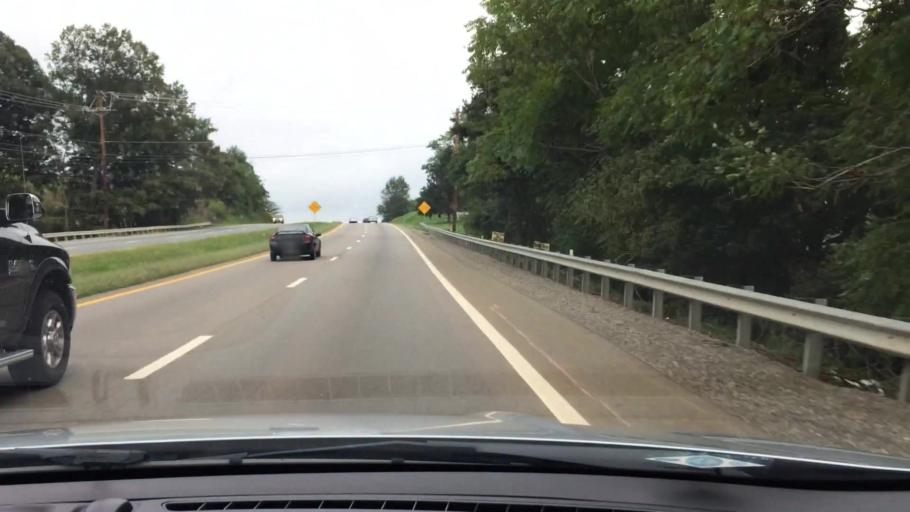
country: US
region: Virginia
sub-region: Franklin County
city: Rocky Mount
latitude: 37.0800
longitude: -79.9209
